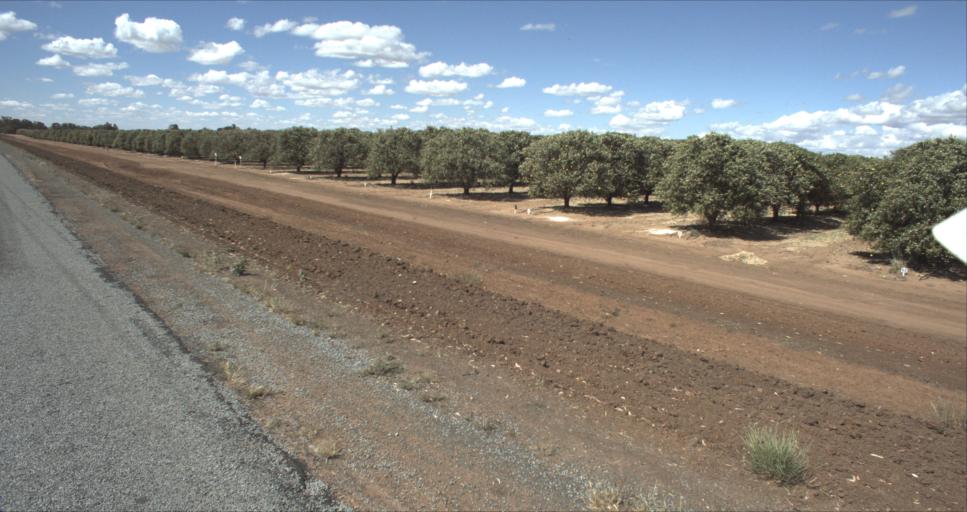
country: AU
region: New South Wales
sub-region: Leeton
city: Leeton
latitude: -34.5223
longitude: 146.2232
